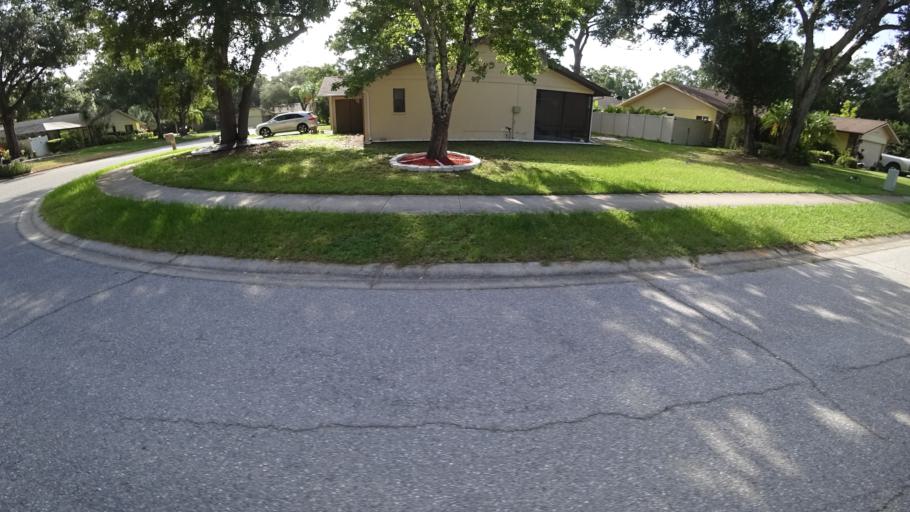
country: US
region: Florida
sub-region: Sarasota County
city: Desoto Lakes
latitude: 27.3908
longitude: -82.5011
